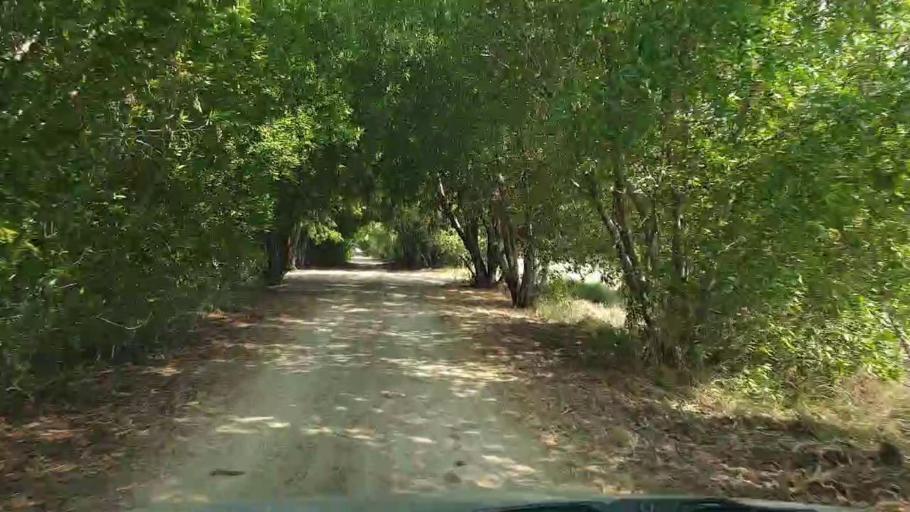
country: PK
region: Sindh
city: Tando Muhammad Khan
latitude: 25.0282
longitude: 68.3994
